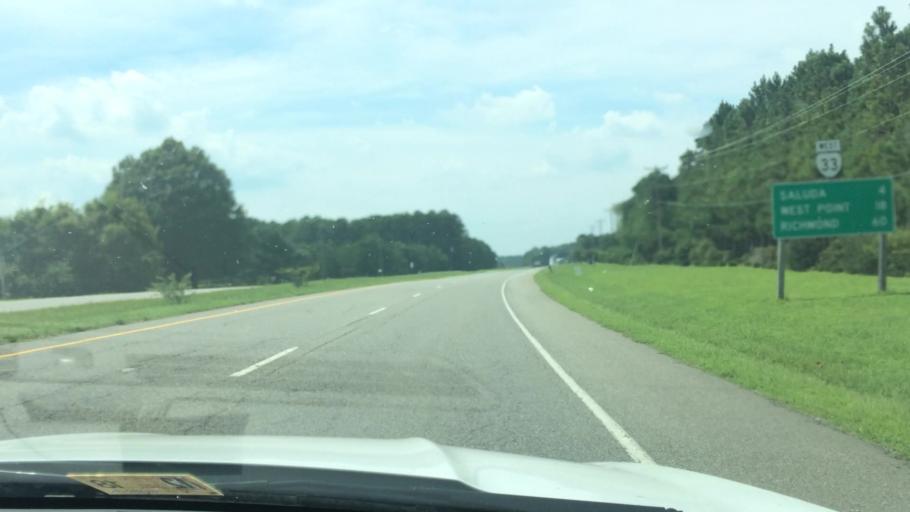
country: US
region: Virginia
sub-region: Middlesex County
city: Saluda
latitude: 37.6038
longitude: -76.5325
